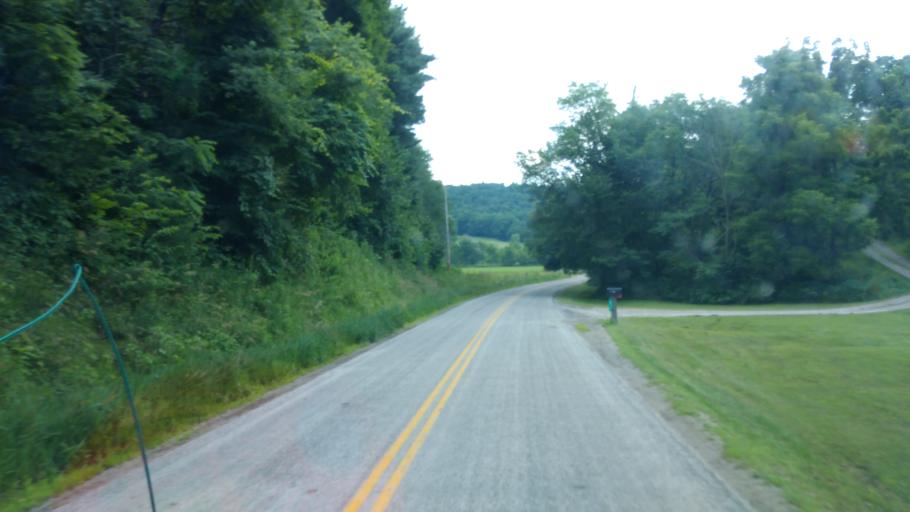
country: US
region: Ohio
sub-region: Ashland County
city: Loudonville
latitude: 40.7310
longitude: -82.2942
